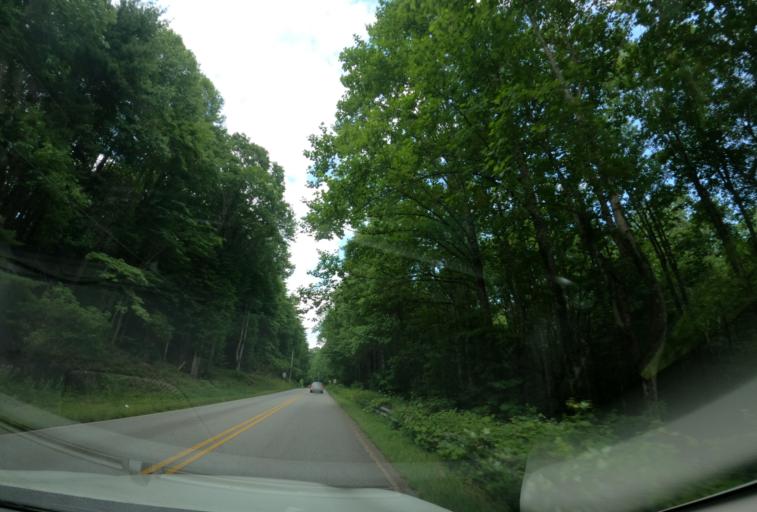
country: US
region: South Carolina
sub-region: Oconee County
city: Walhalla
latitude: 35.0544
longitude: -83.0111
